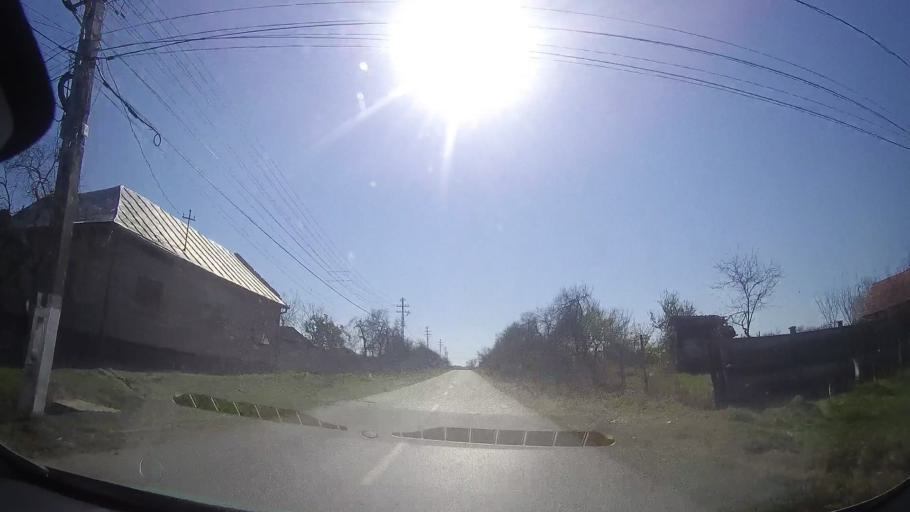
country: RO
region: Timis
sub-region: Comuna Bethausen
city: Bethausen
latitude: 45.7957
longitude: 21.9645
